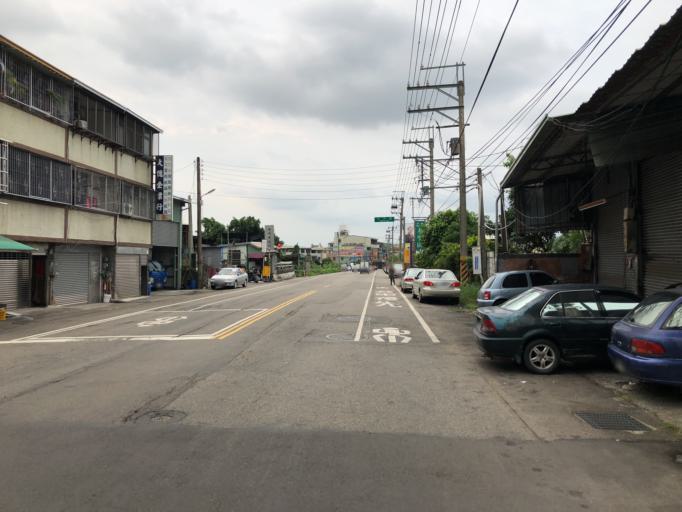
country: TW
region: Taiwan
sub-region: Taichung City
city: Taichung
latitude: 24.0940
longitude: 120.7292
